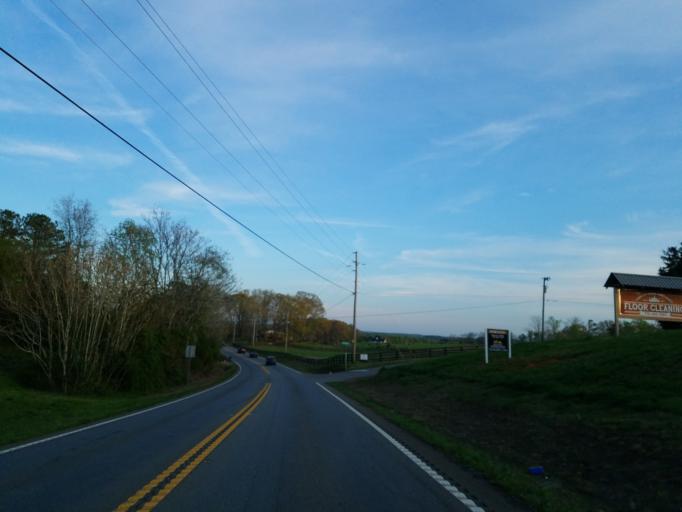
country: US
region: Georgia
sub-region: Cherokee County
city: Holly Springs
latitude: 34.1918
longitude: -84.4428
